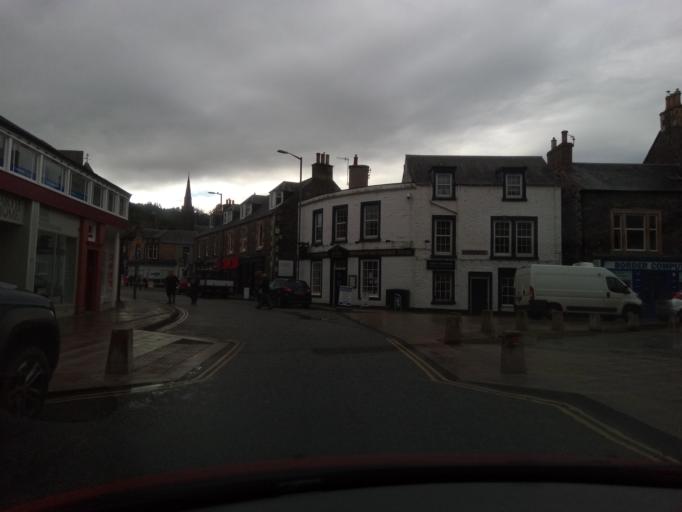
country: GB
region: Scotland
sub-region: The Scottish Borders
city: Galashiels
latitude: 55.6156
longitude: -2.8059
